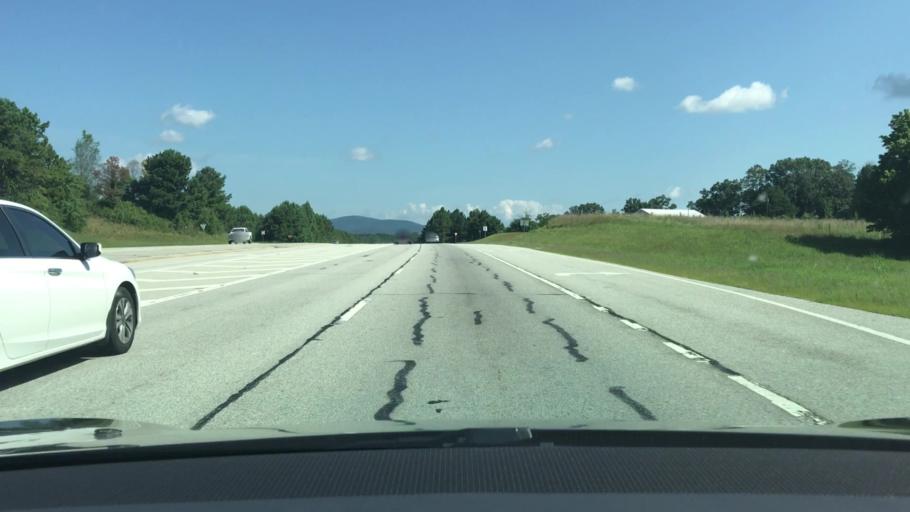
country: US
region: Georgia
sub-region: Habersham County
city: Clarkesville
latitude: 34.6256
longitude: -83.4474
